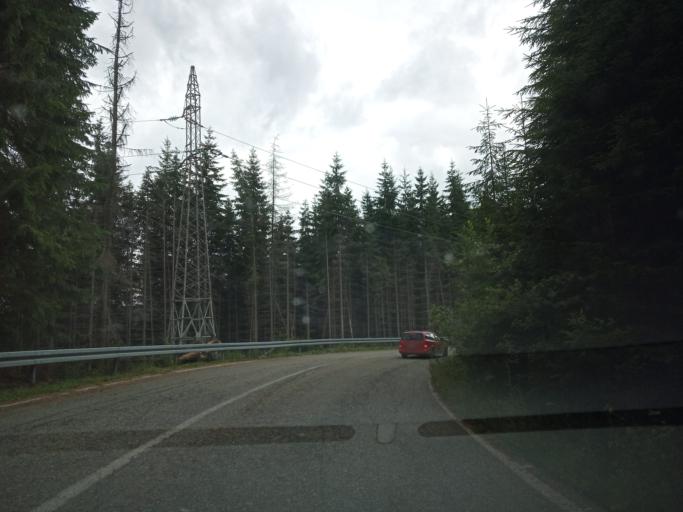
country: RO
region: Valcea
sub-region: Comuna Voineasa
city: Voineasa
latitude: 45.4198
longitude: 23.7391
